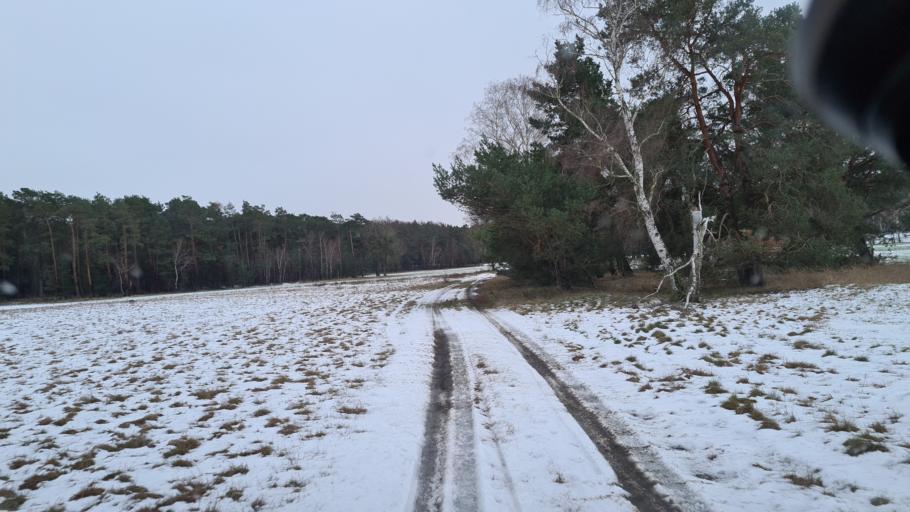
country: DE
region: Brandenburg
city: Schenkendobern
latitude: 51.9028
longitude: 14.5946
